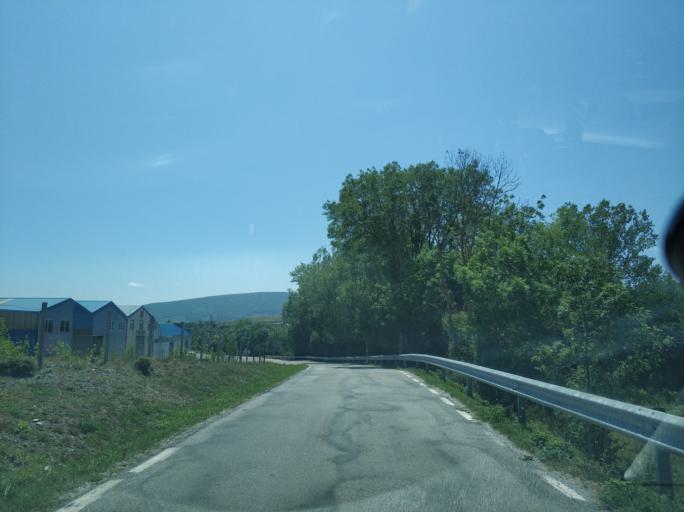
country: ES
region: Cantabria
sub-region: Provincia de Cantabria
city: Reinosa
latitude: 43.0105
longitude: -4.1664
